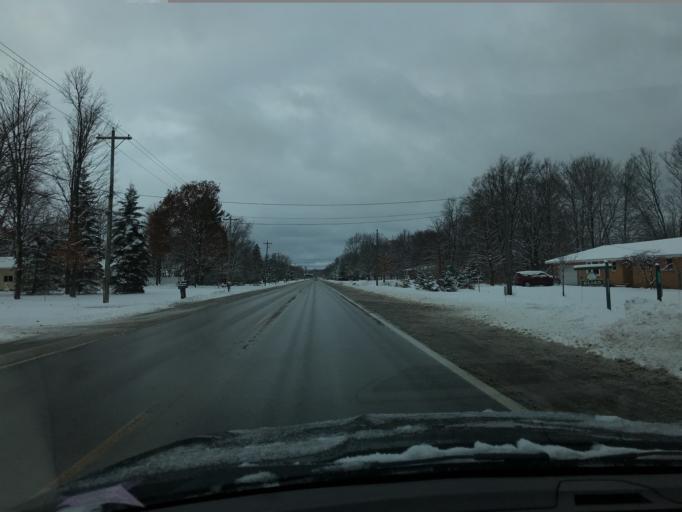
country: US
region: Michigan
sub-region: Charlevoix County
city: Charlevoix
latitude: 45.2887
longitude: -85.2458
